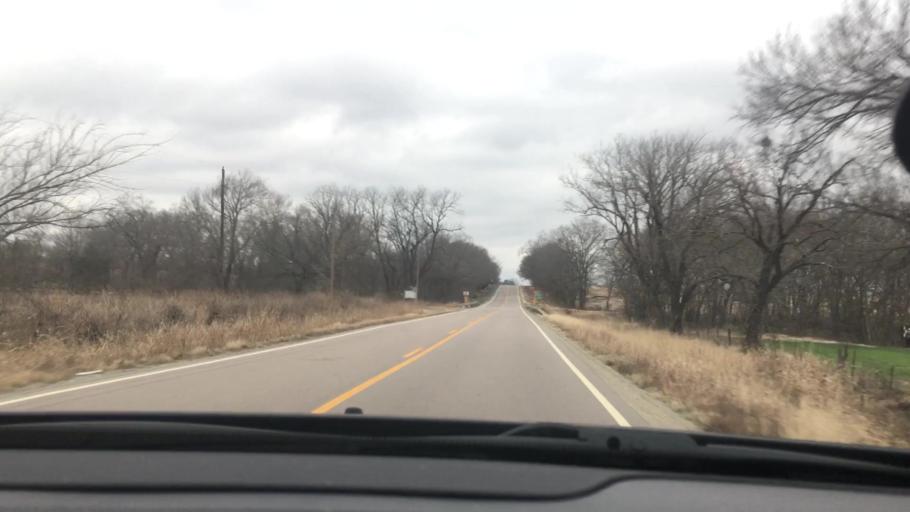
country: US
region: Oklahoma
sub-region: Coal County
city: Coalgate
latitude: 34.3718
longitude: -96.3534
